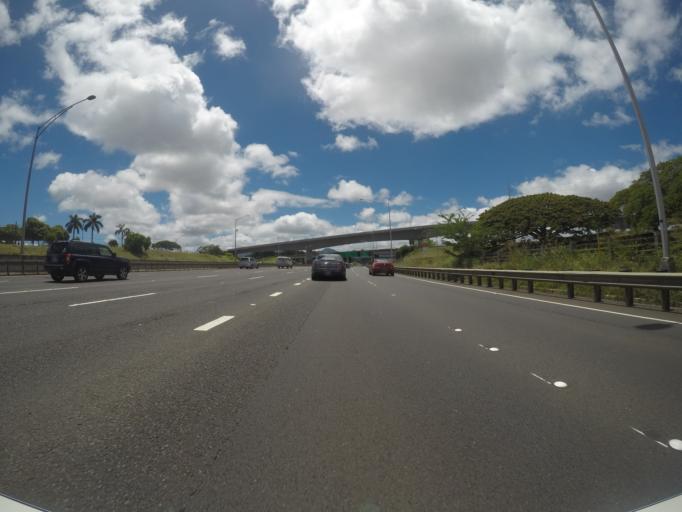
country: US
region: Hawaii
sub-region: Honolulu County
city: Pearl City, Manana
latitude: 21.3950
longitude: -157.9823
